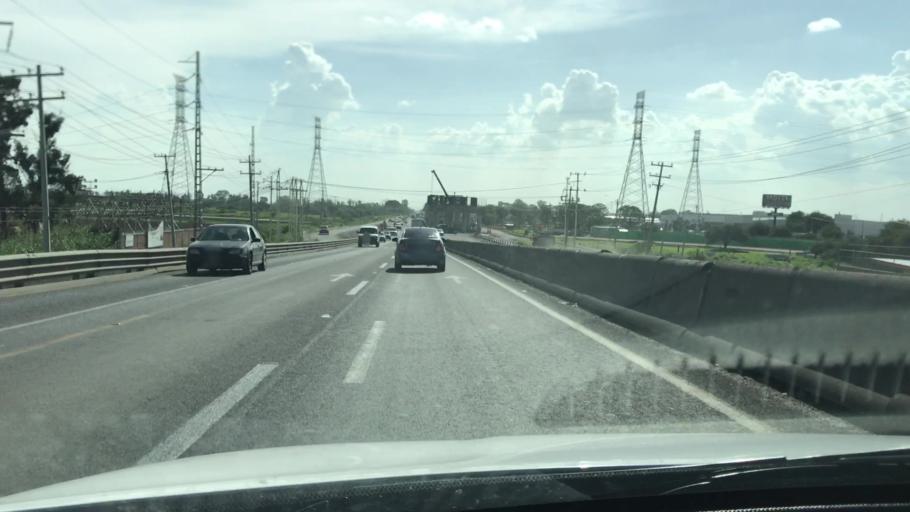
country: MX
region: Guanajuato
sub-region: Celaya
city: Colonia Fraccionamiento el Puente
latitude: 20.5152
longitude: -100.8971
